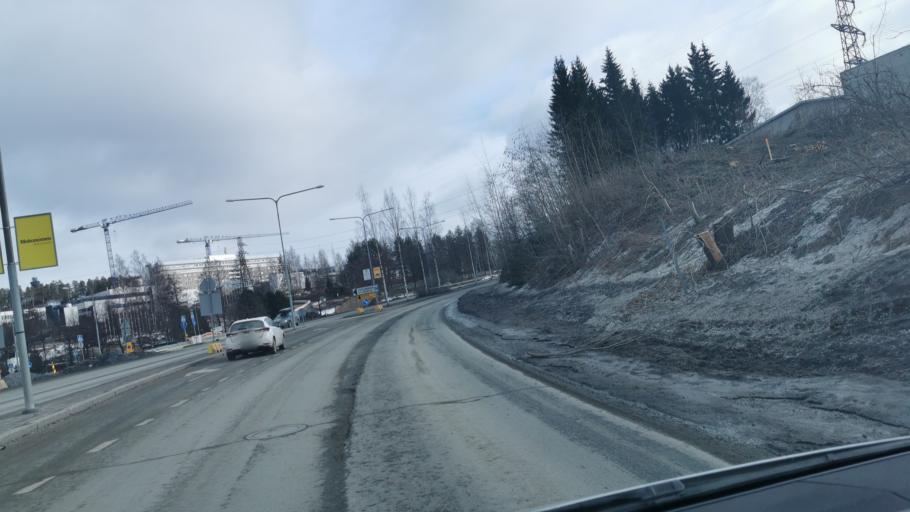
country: FI
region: Northern Savo
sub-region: Kuopio
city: Kuopio
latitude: 62.8936
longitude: 27.6409
